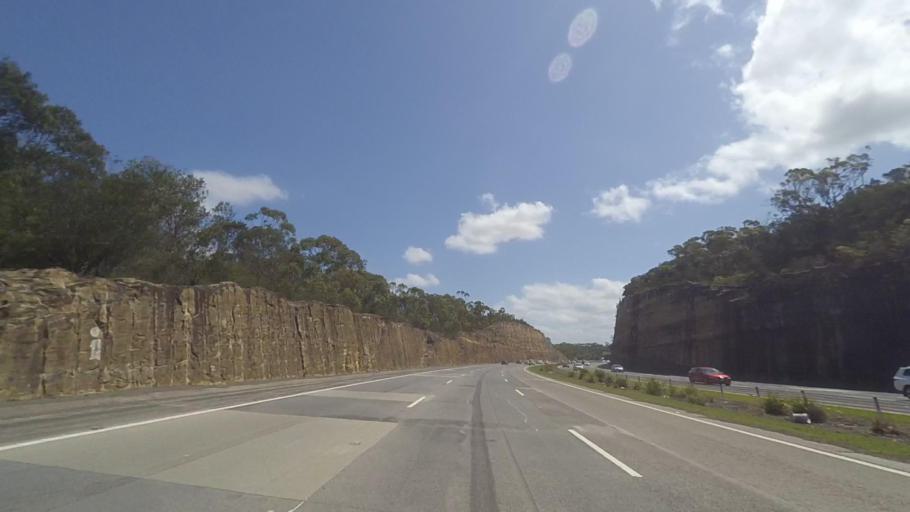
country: AU
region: New South Wales
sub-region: Hornsby Shire
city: Berowra
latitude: -33.6414
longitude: 151.1441
